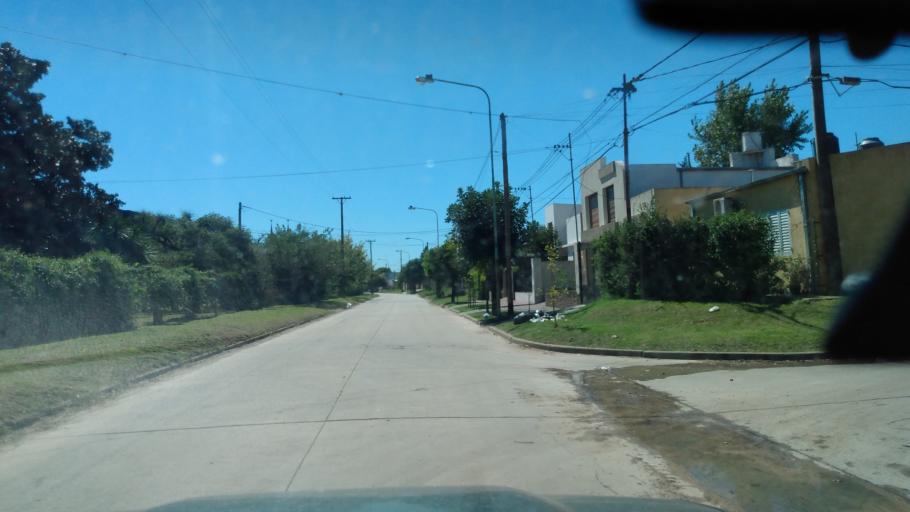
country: AR
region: Buenos Aires
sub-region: Partido de Lujan
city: Lujan
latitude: -34.5733
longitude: -59.1249
